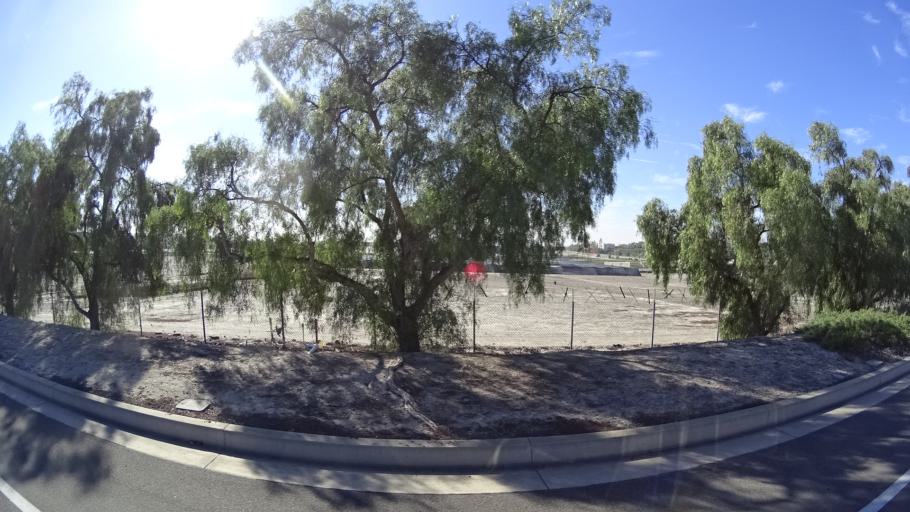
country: US
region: California
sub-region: Orange County
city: Foothill Ranch
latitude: 33.6716
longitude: -117.6651
